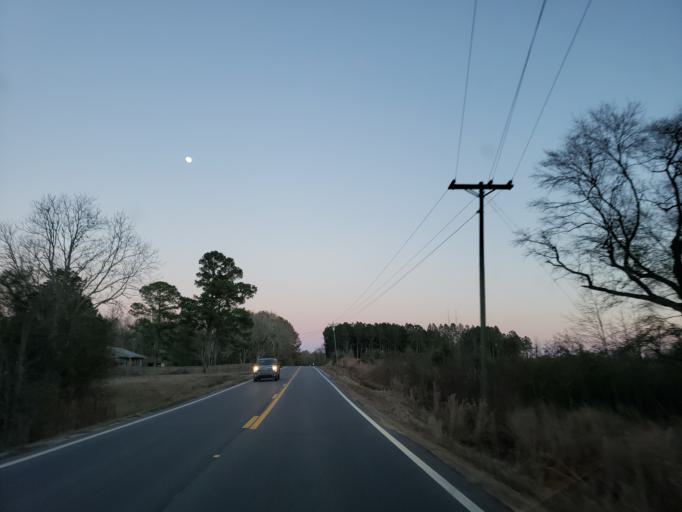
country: US
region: Mississippi
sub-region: Jones County
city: Ellisville
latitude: 31.5797
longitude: -89.2585
